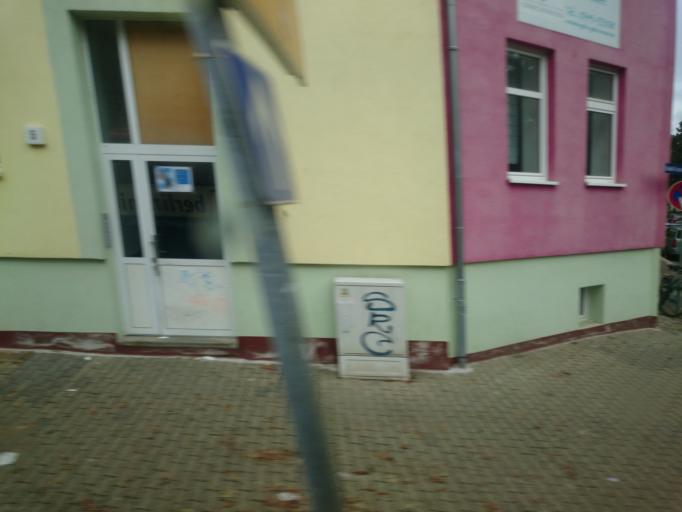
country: DE
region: Saxony-Anhalt
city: Halle (Saale)
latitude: 51.4749
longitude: 11.9851
